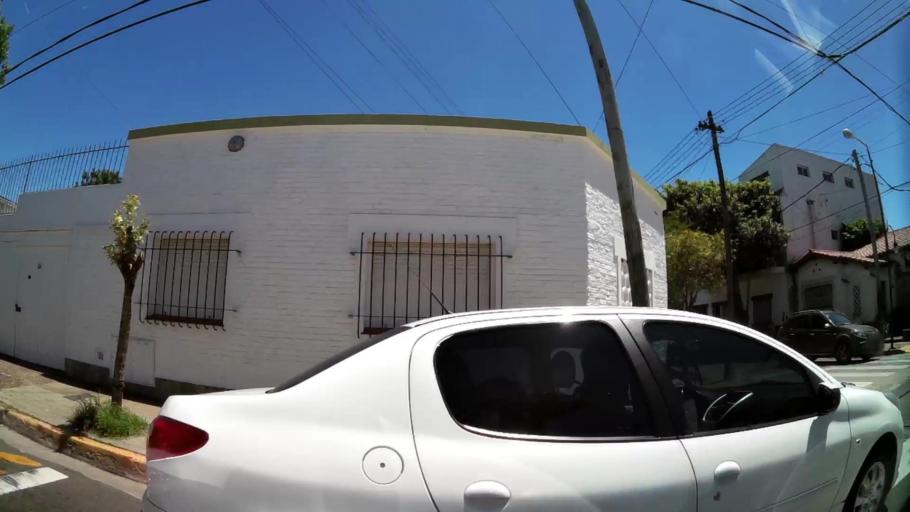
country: AR
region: Buenos Aires
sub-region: Partido de Tigre
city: Tigre
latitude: -34.4487
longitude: -58.5486
